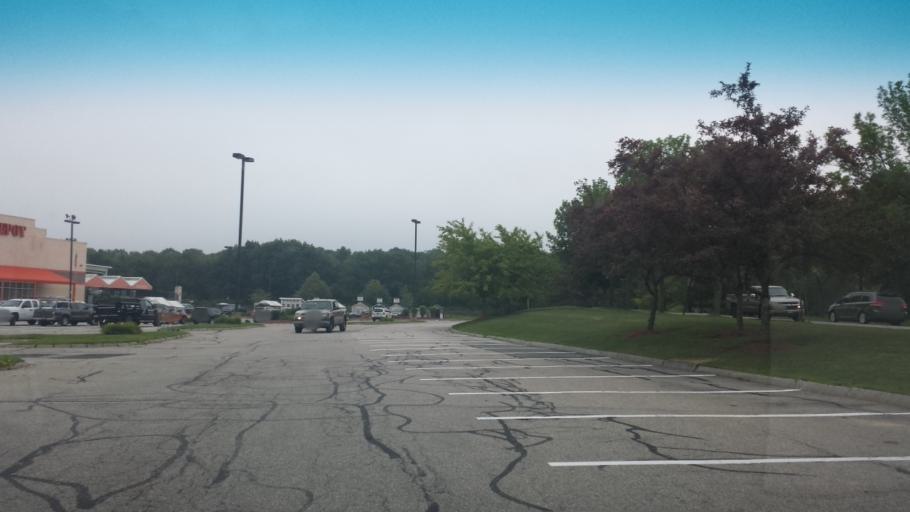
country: US
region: Maine
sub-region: Cumberland County
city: South Portland Gardens
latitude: 43.6321
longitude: -70.3224
